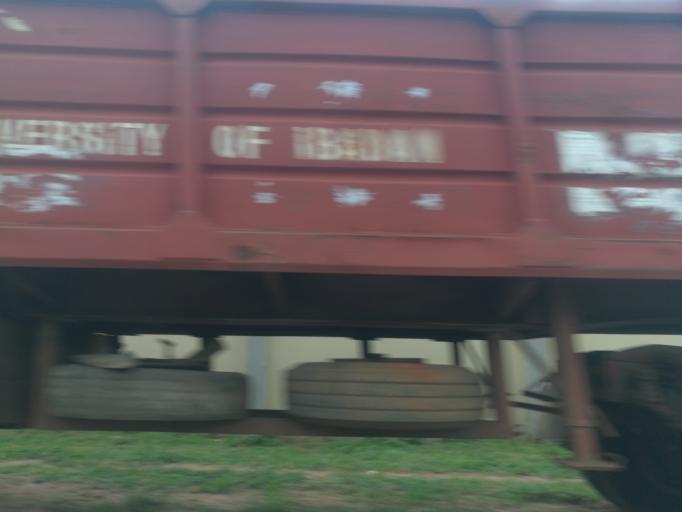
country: NG
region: Oyo
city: Ibadan
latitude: 7.4508
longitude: 3.9027
